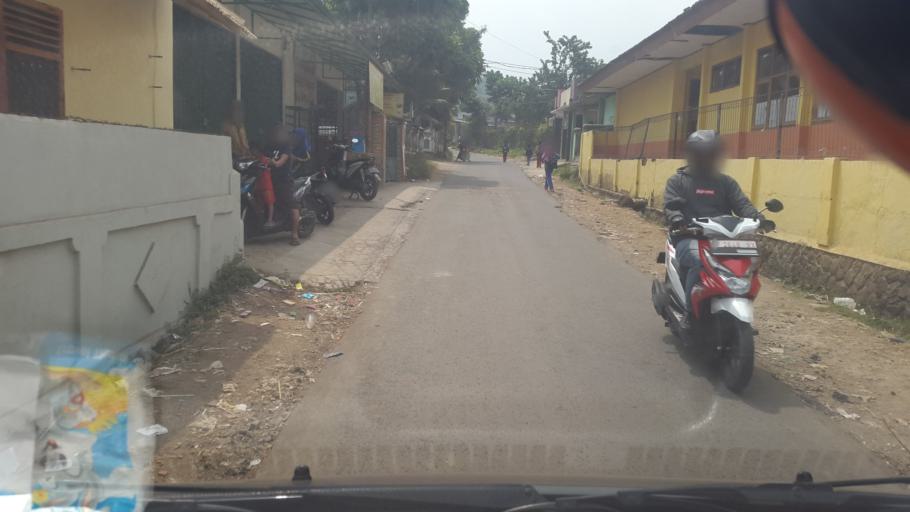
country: ID
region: West Java
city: Sukabumi
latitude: -6.8682
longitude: 106.8953
